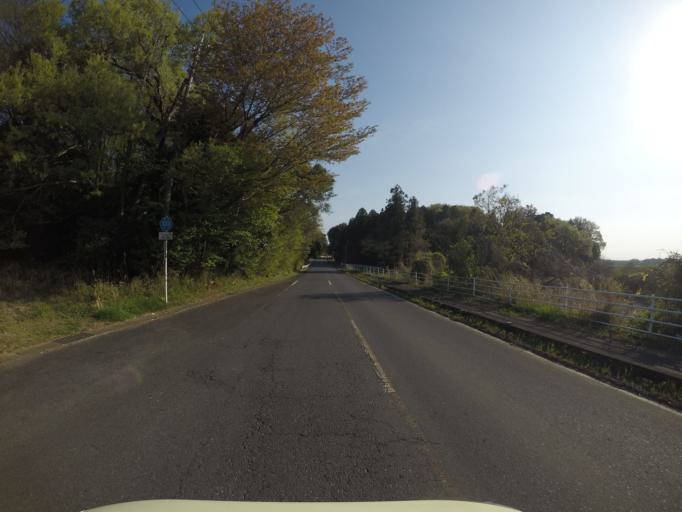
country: JP
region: Ibaraki
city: Ishige
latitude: 36.1754
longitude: 140.0182
